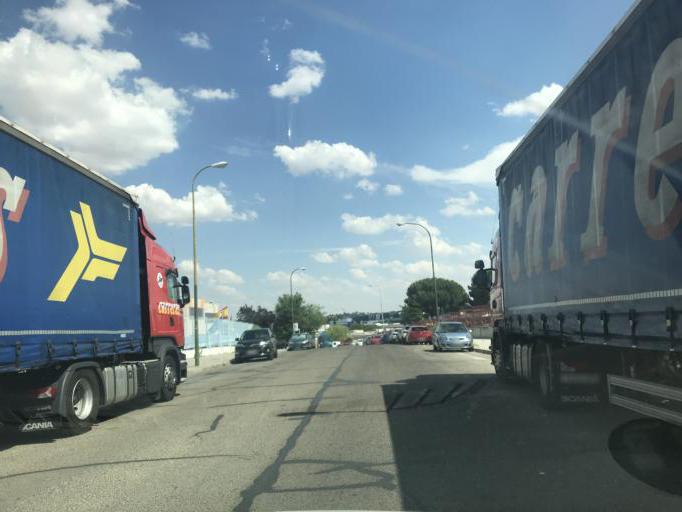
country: ES
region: Madrid
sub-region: Provincia de Madrid
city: Alcobendas
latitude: 40.5372
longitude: -3.6543
